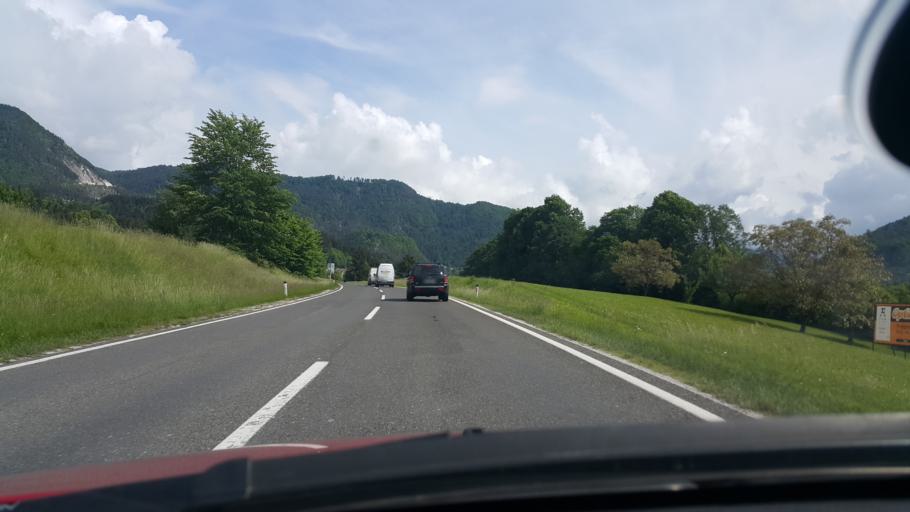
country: SI
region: Trzic
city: Bistrica pri Trzicu
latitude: 46.3417
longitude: 14.2861
